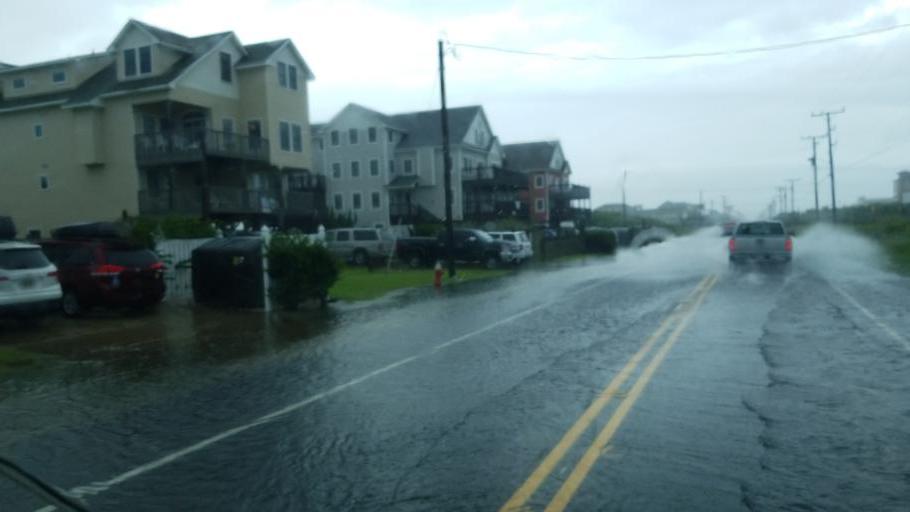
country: US
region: North Carolina
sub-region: Dare County
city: Kill Devil Hills
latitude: 36.0236
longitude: -75.6631
